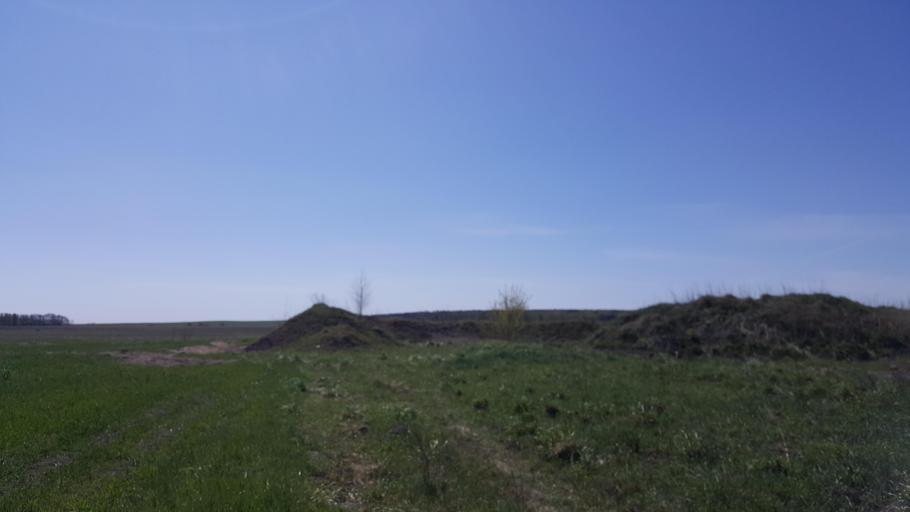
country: BY
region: Brest
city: Charnawchytsy
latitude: 52.3176
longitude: 23.7224
